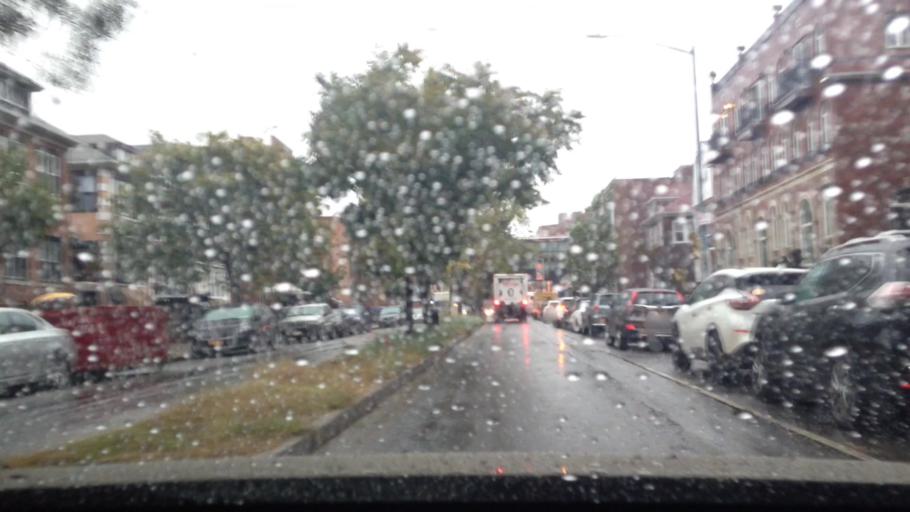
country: US
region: New York
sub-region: Queens County
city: Long Island City
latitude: 40.7484
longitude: -73.8908
